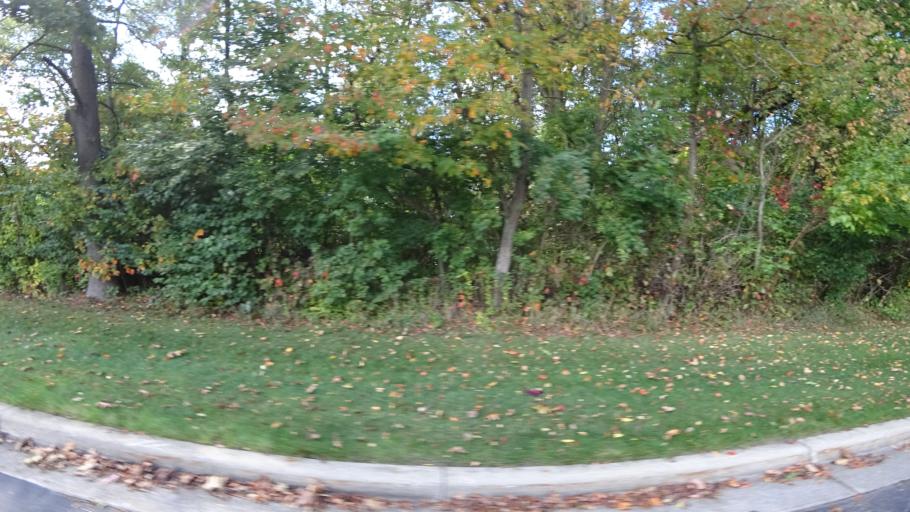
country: US
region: Michigan
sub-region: Saint Joseph County
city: Three Rivers
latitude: 41.9562
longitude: -85.6139
